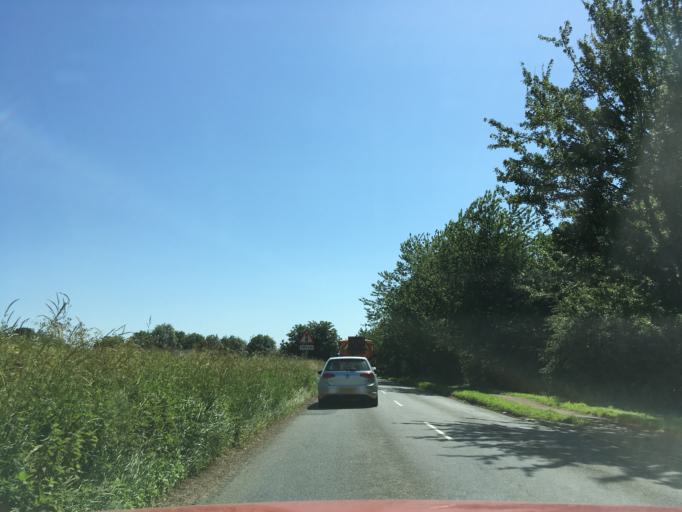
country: GB
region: England
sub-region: Oxfordshire
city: Deddington
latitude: 51.9828
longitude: -1.3338
